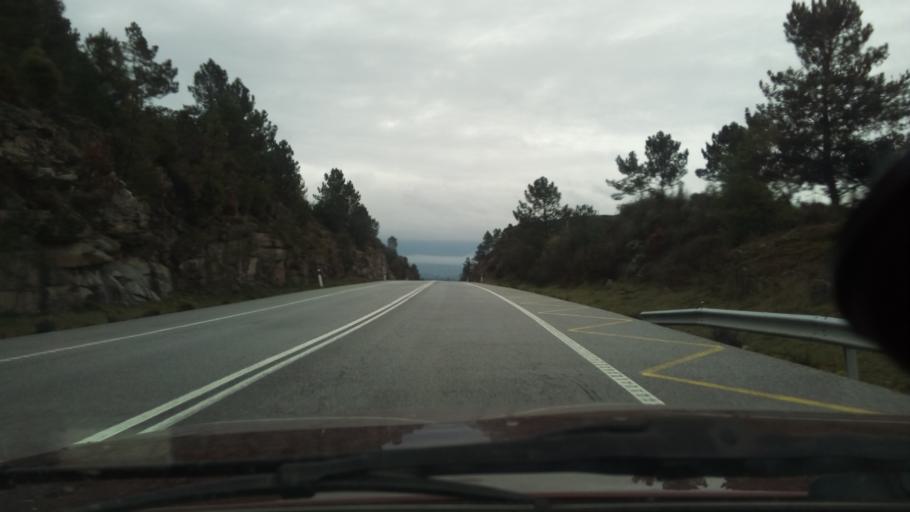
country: PT
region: Guarda
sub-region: Fornos de Algodres
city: Fornos de Algodres
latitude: 40.6058
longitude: -7.5874
